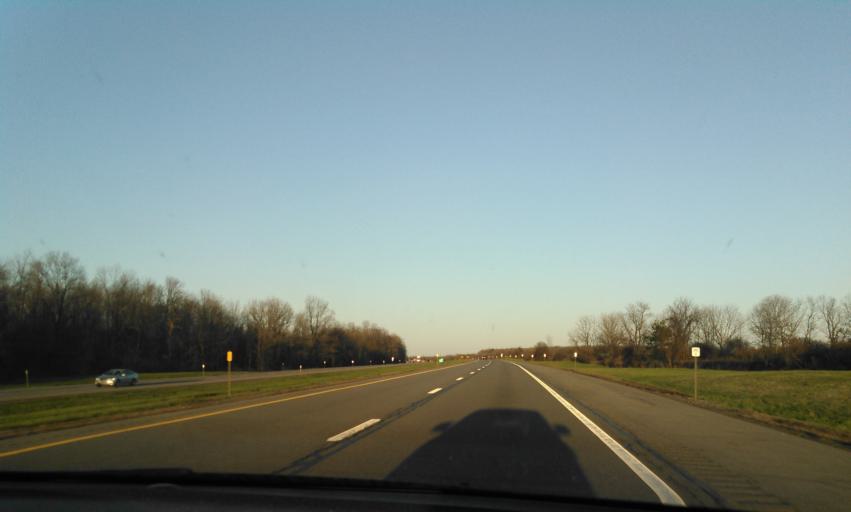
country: US
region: New York
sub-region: Ontario County
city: Manchester
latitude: 42.9802
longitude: -77.2731
